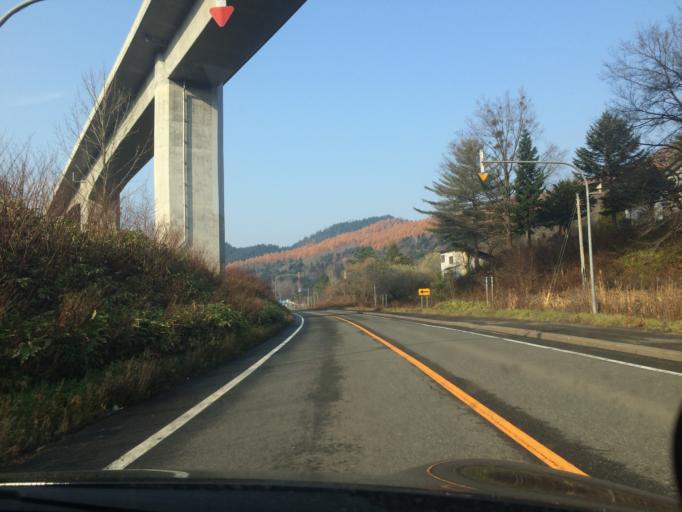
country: JP
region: Hokkaido
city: Iwamizawa
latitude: 42.9338
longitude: 142.0820
